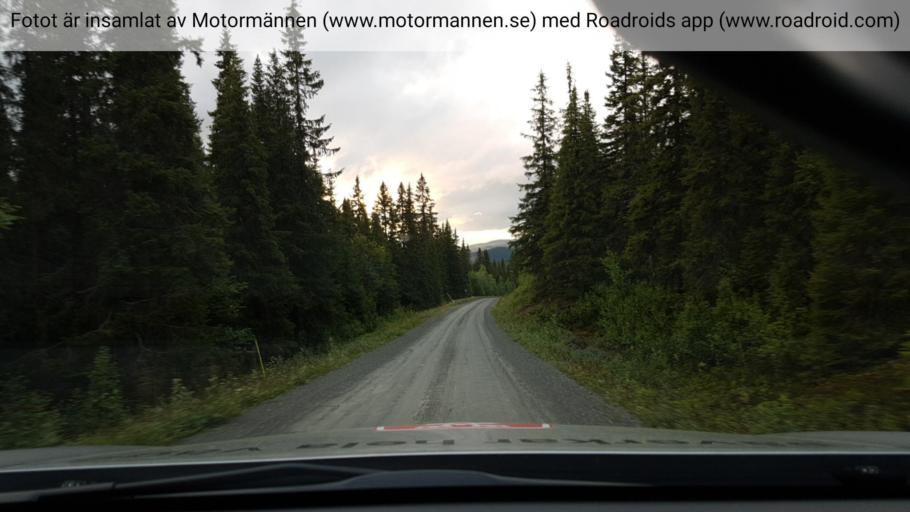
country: SE
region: Vaesterbotten
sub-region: Vilhelmina Kommun
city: Sjoberg
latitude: 65.4956
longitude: 15.4900
